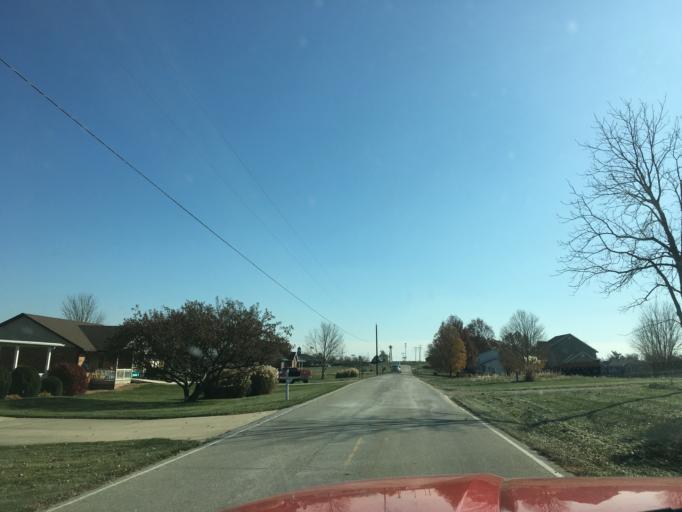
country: US
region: Missouri
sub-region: Cole County
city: Wardsville
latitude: 38.4992
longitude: -92.1821
